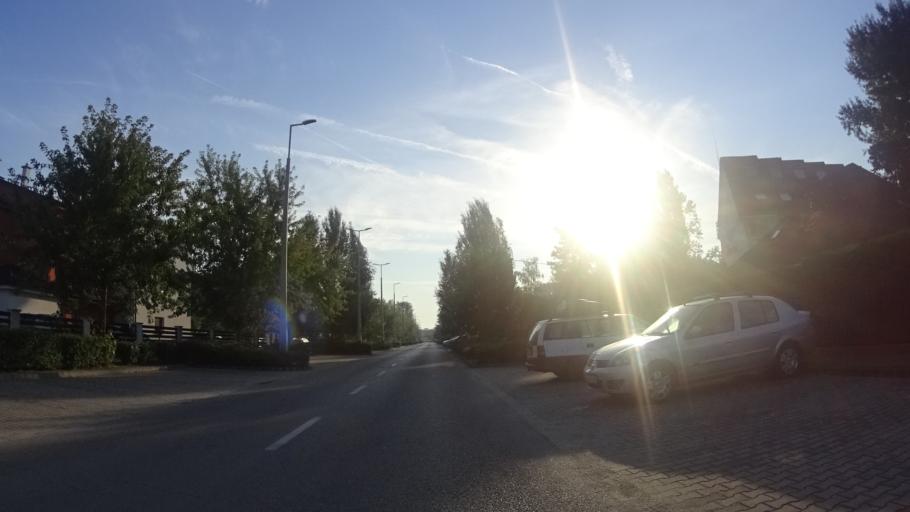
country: HU
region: Somogy
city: Siofok
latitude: 46.9237
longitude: 18.0917
